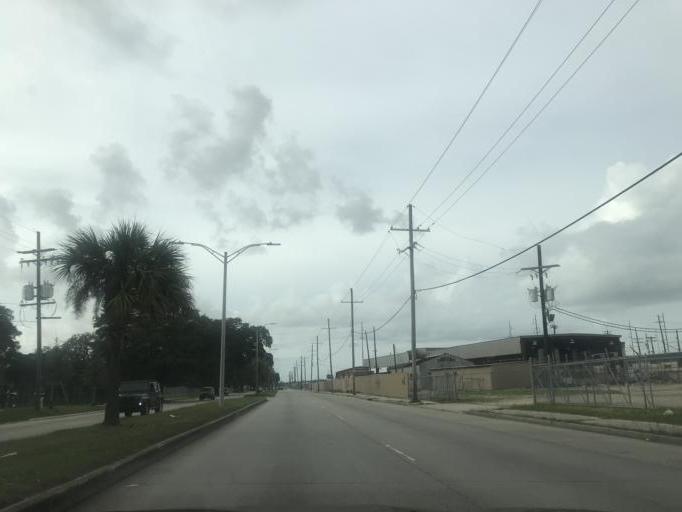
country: US
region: Louisiana
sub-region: Orleans Parish
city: New Orleans
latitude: 29.9506
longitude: -90.0886
